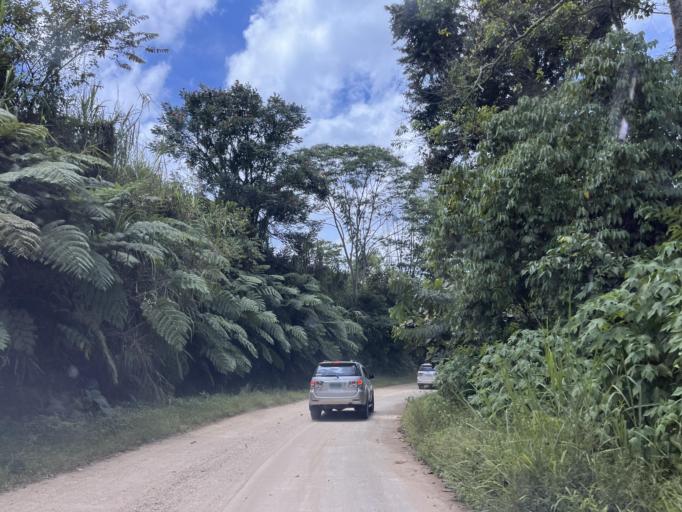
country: PH
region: Northern Mindanao
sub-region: Province of Bukidnon
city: Sumilao
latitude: 8.2832
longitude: 124.9438
